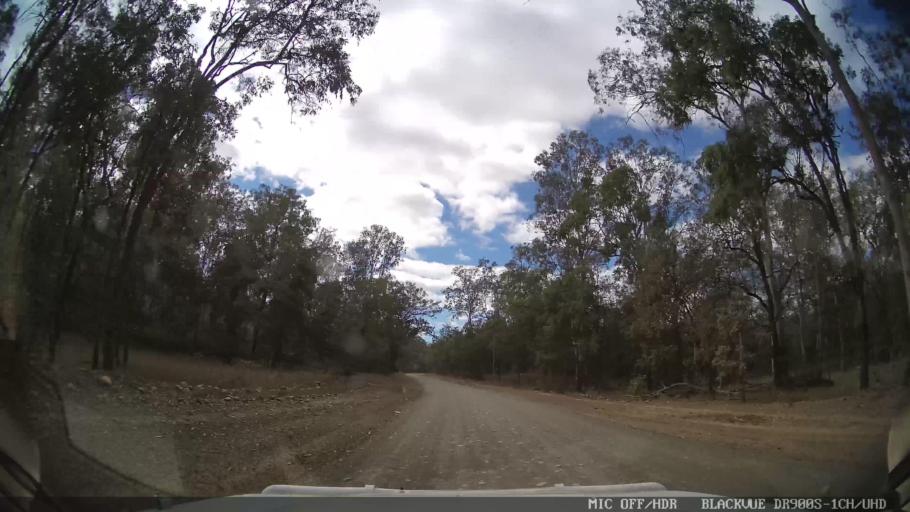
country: AU
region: Queensland
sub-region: Gladstone
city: Toolooa
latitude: -24.5497
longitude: 151.3423
